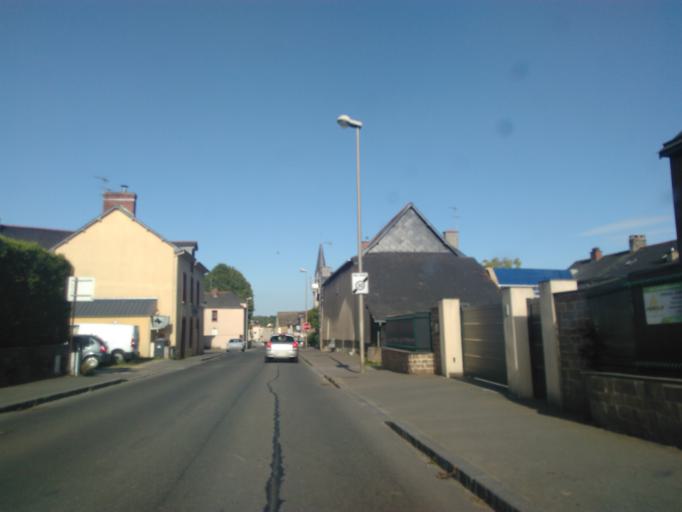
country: FR
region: Brittany
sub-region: Departement d'Ille-et-Vilaine
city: Geveze
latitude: 48.2214
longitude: -1.7927
